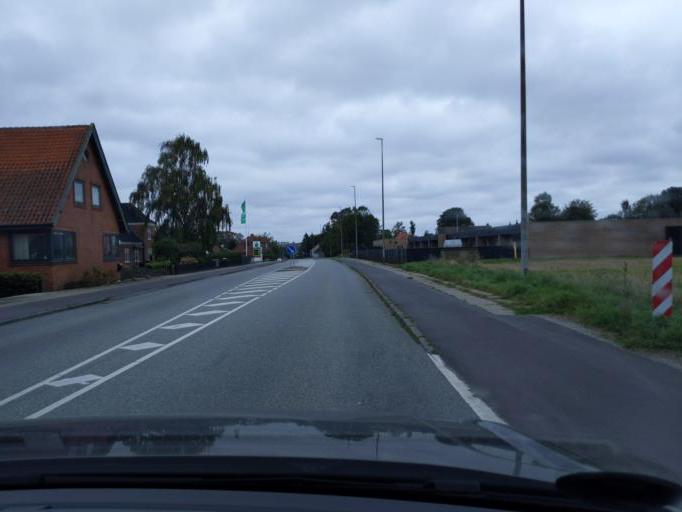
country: DK
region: Central Jutland
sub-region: Randers Kommune
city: Spentrup
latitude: 56.5113
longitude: 9.9516
